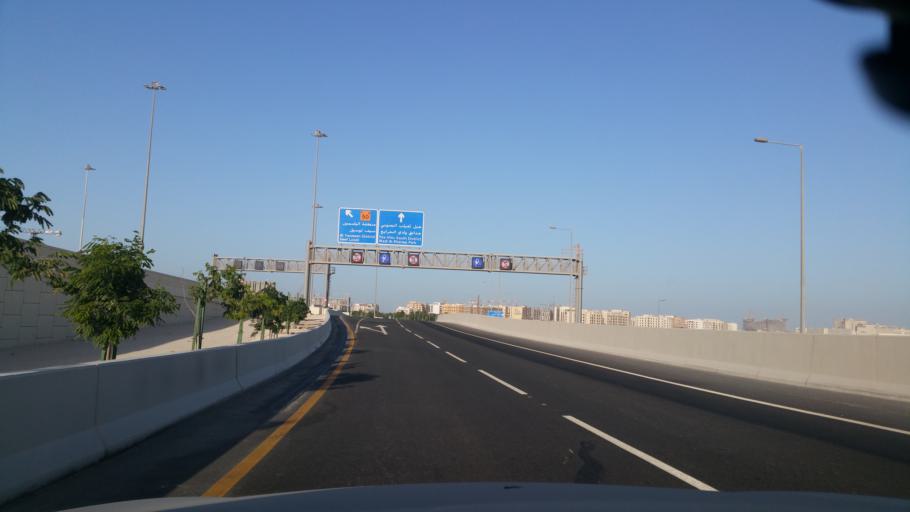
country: QA
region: Baladiyat Umm Salal
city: Umm Salal Muhammad
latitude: 25.4047
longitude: 51.4928
